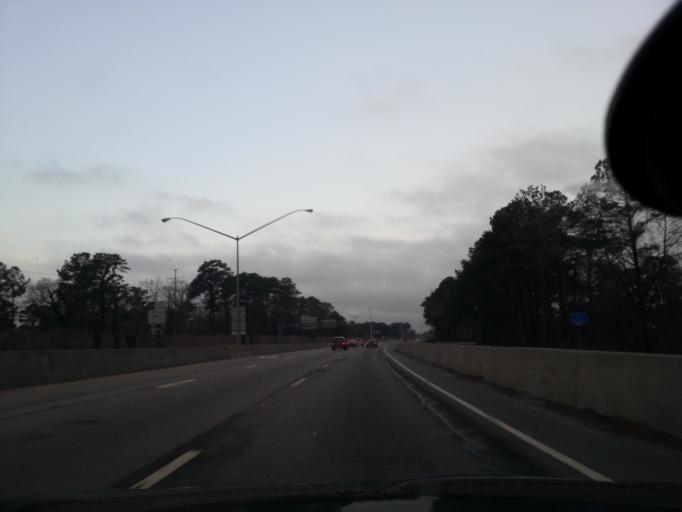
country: US
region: Virginia
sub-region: City of Chesapeake
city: Chesapeake
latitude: 36.8425
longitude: -76.2145
